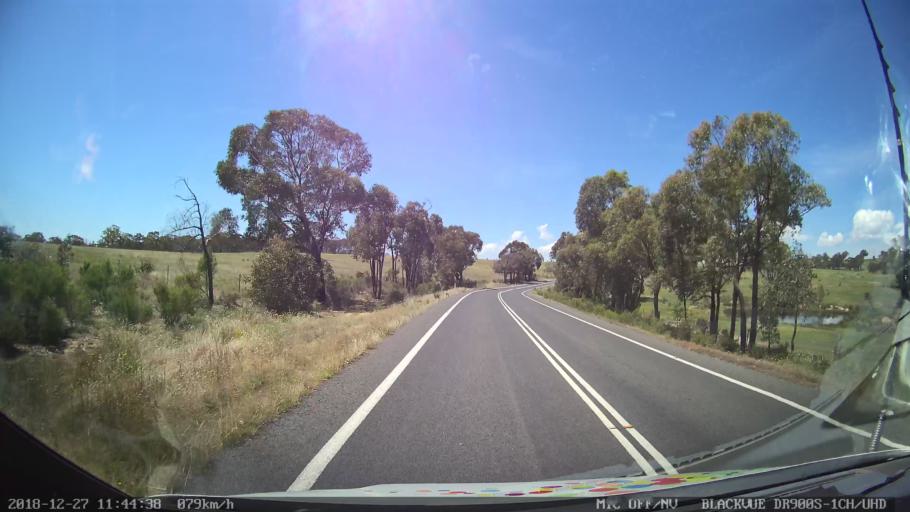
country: AU
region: New South Wales
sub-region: Bathurst Regional
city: Perthville
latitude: -33.5745
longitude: 149.4758
